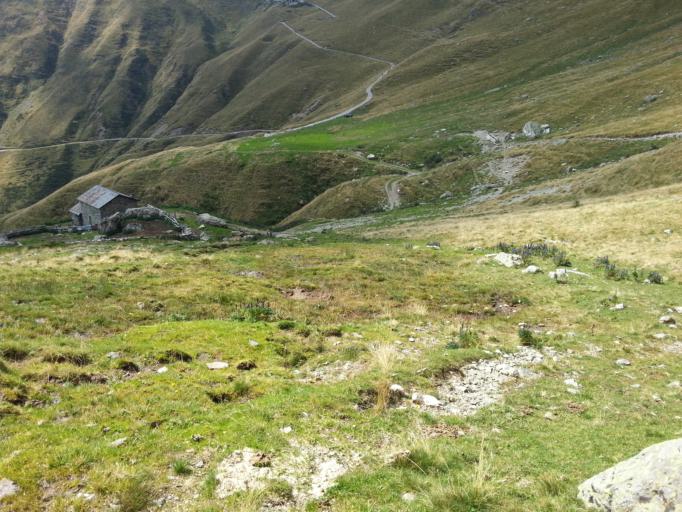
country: CH
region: Grisons
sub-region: Moesa District
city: Roveredo
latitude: 46.1664
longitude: 9.1682
